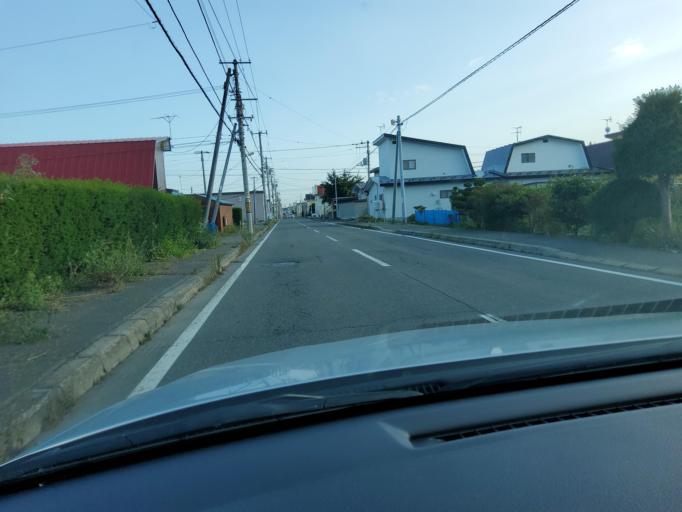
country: JP
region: Hokkaido
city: Obihiro
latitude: 42.9376
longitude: 143.1828
